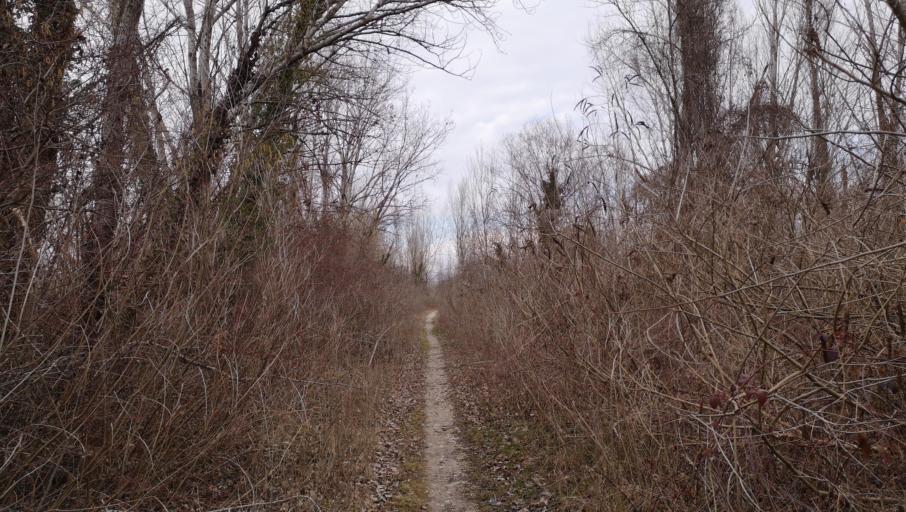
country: IT
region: Friuli Venezia Giulia
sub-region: Provincia di Udine
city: Povoletto
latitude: 46.1062
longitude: 13.2776
